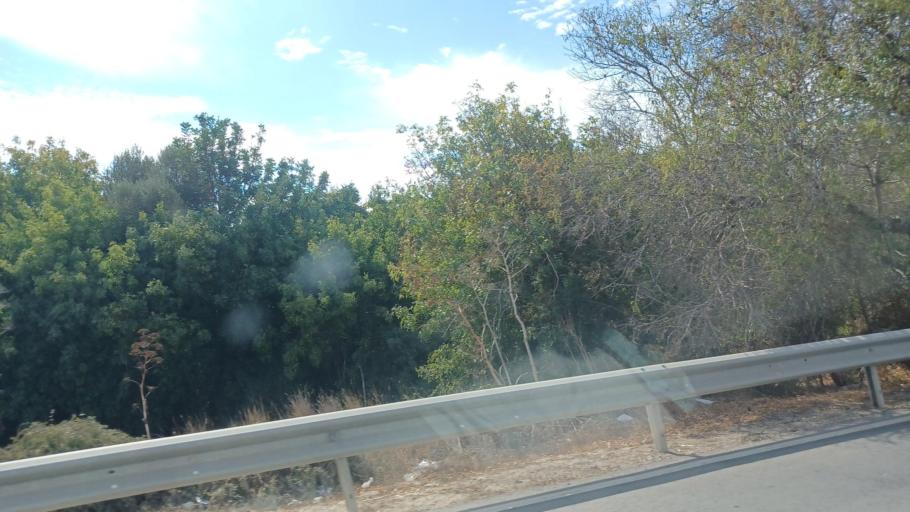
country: CY
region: Pafos
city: Mesogi
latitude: 34.8028
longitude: 32.4552
